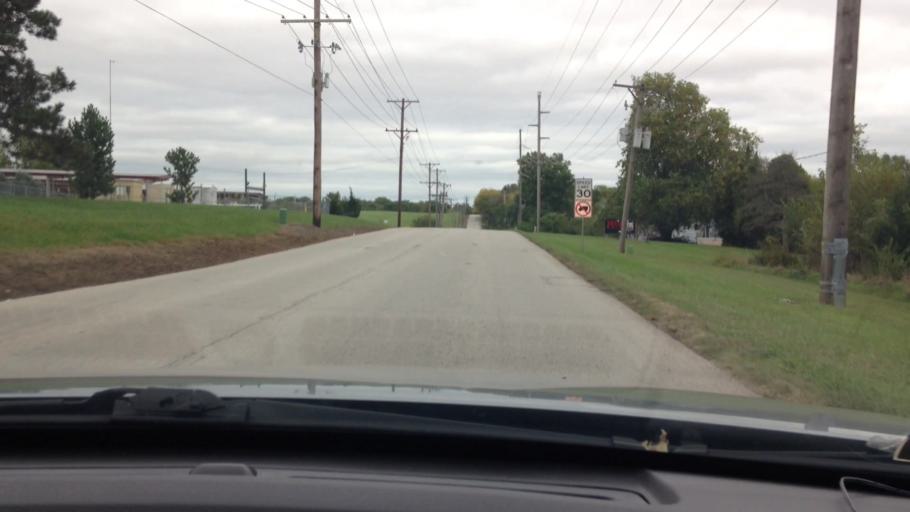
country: US
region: Kansas
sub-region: Leavenworth County
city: Lansing
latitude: 39.2741
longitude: -94.9088
